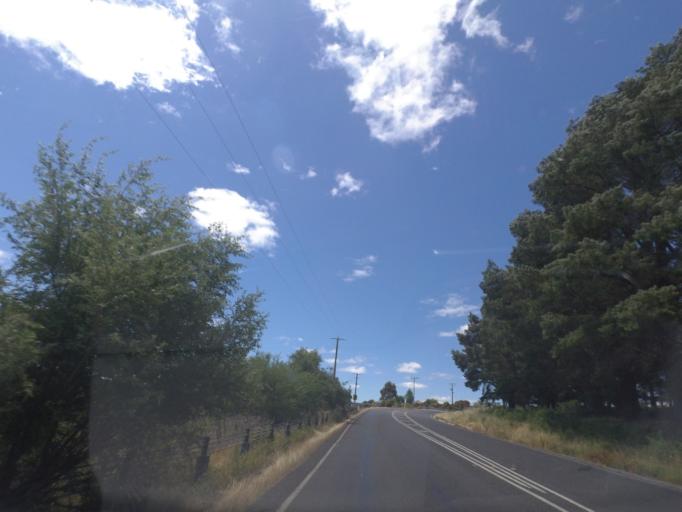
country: AU
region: Victoria
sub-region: Mount Alexander
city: Castlemaine
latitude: -37.3243
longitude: 144.1940
